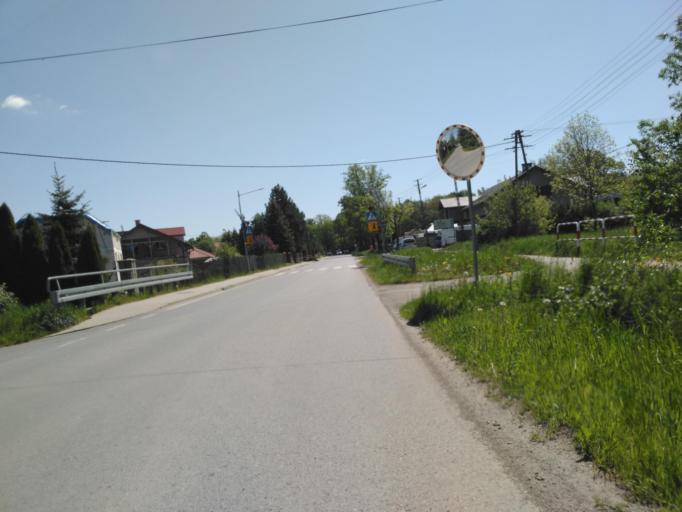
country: PL
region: Subcarpathian Voivodeship
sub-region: Powiat krosnienski
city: Miejsce Piastowe
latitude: 49.6037
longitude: 21.7940
